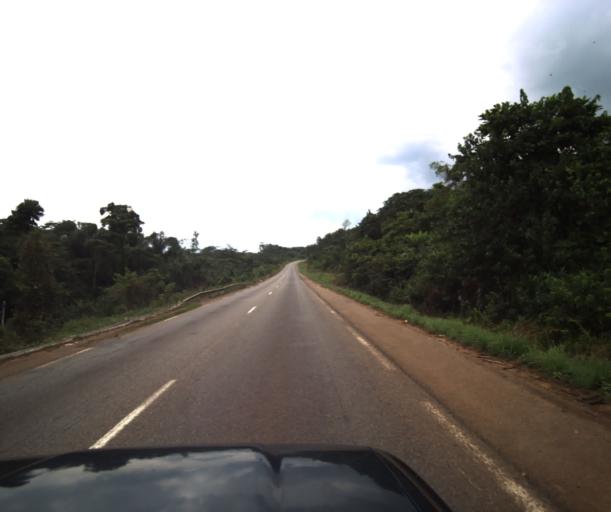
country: CM
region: Littoral
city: Edea
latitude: 3.8726
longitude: 10.0720
